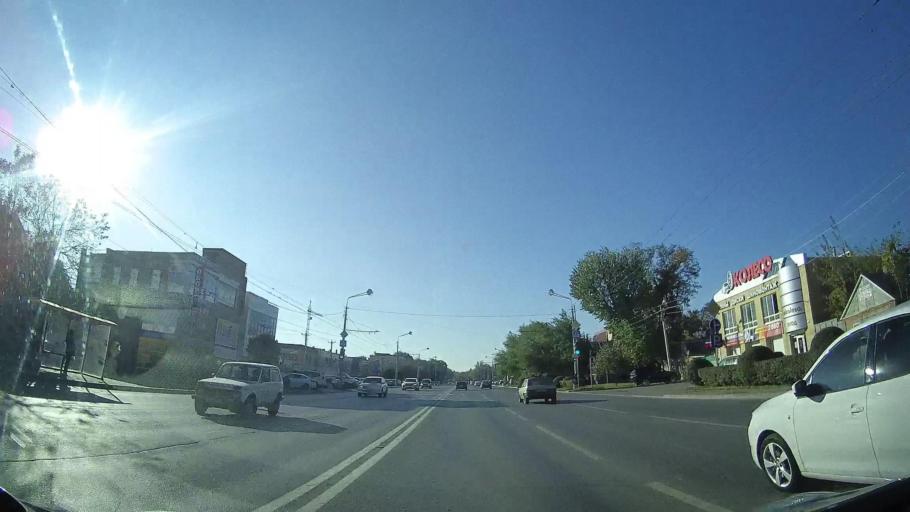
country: RU
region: Rostov
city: Rostov-na-Donu
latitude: 47.2119
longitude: 39.6533
